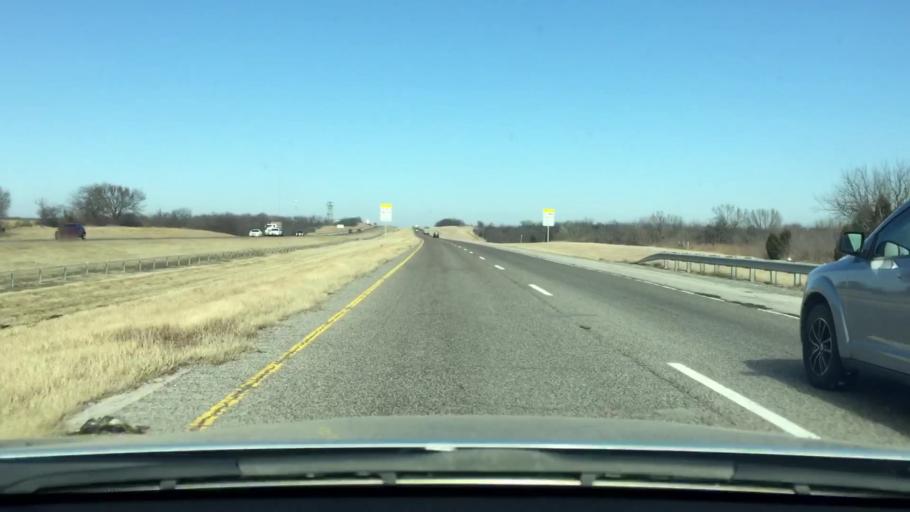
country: US
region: Oklahoma
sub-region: McClain County
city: Purcell
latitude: 34.9249
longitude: -97.3590
